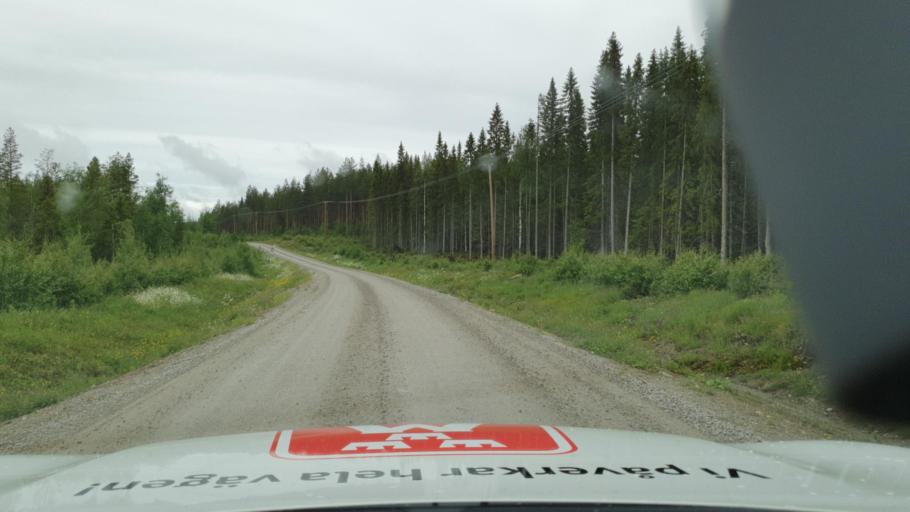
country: SE
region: Vaesterbotten
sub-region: Asele Kommun
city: Asele
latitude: 63.9694
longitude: 17.0711
